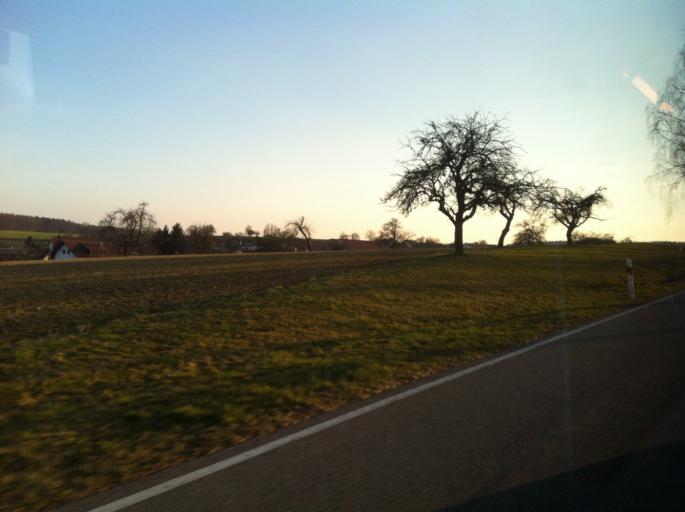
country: DE
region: Baden-Wuerttemberg
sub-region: Karlsruhe Region
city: Fahrenbach
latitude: 49.4747
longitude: 9.1432
